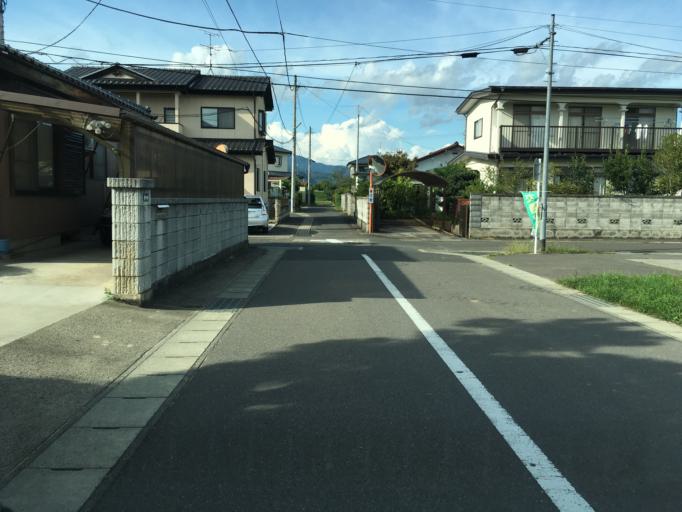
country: JP
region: Fukushima
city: Hobaramachi
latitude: 37.8232
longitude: 140.5162
